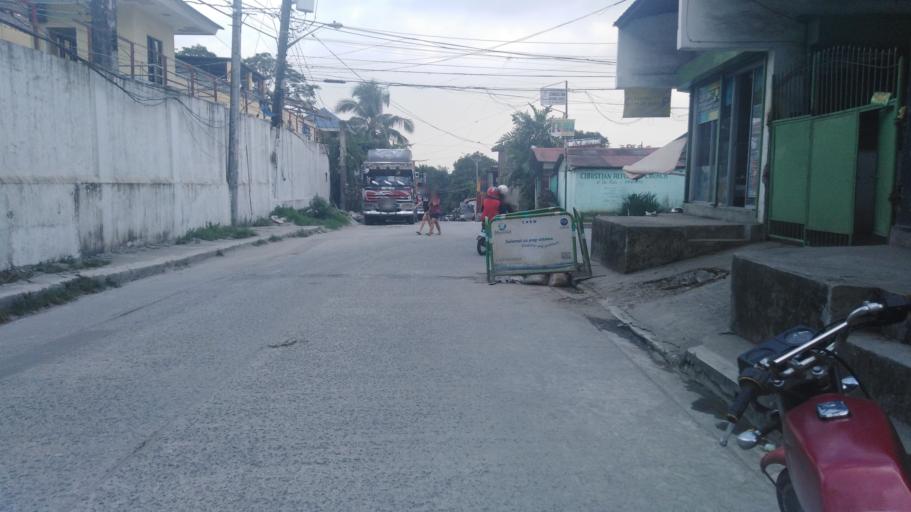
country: PH
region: Calabarzon
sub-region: Province of Rizal
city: San Mateo
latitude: 14.7116
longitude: 121.0956
